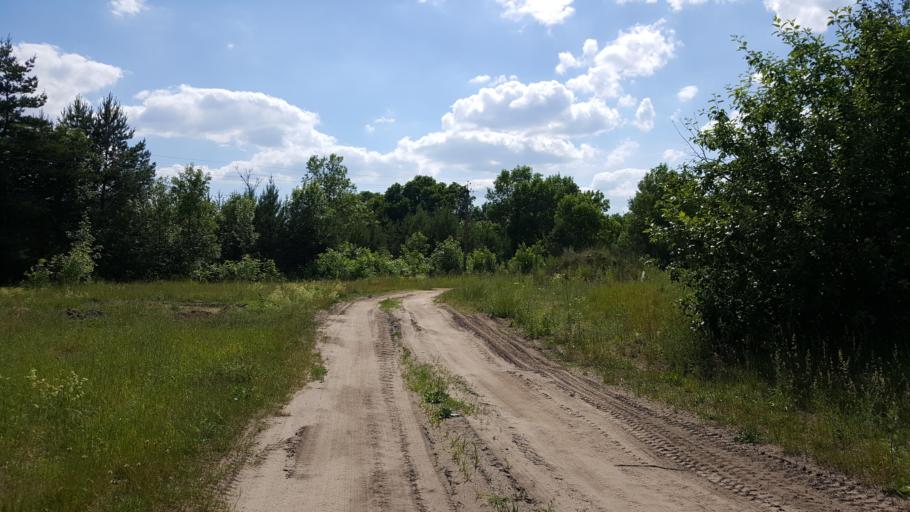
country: BY
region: Brest
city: Kamyanyuki
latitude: 52.5020
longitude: 23.7057
